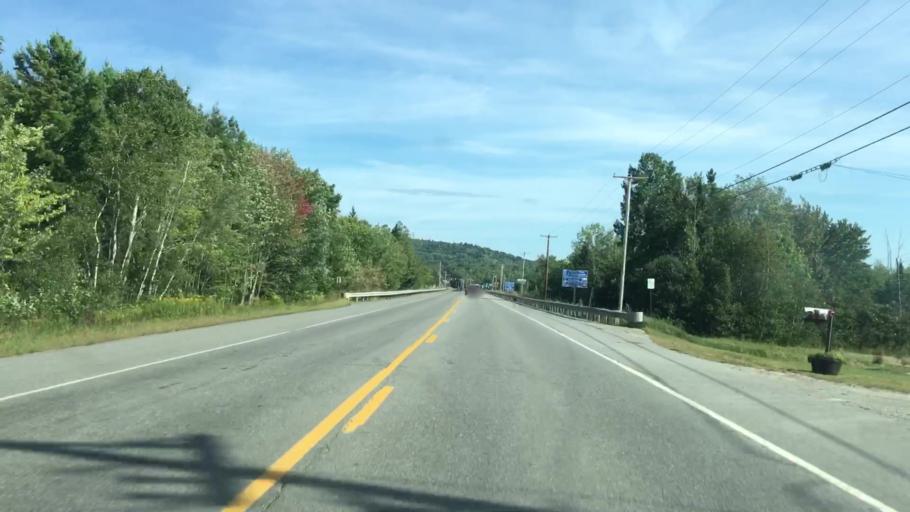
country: US
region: Maine
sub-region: Penobscot County
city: Lincoln
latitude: 45.3565
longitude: -68.5392
